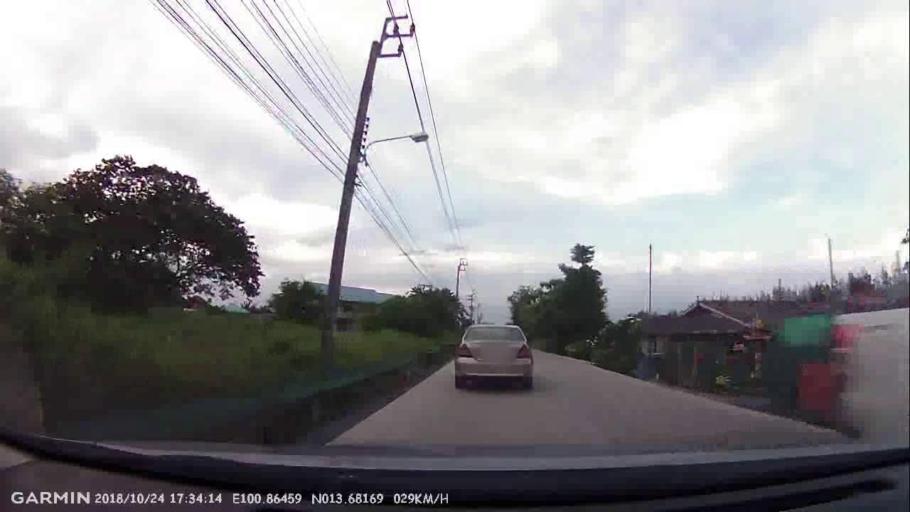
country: TH
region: Samut Prakan
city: Ban Khlong Bang Sao Thong
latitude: 13.6817
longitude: 100.8646
